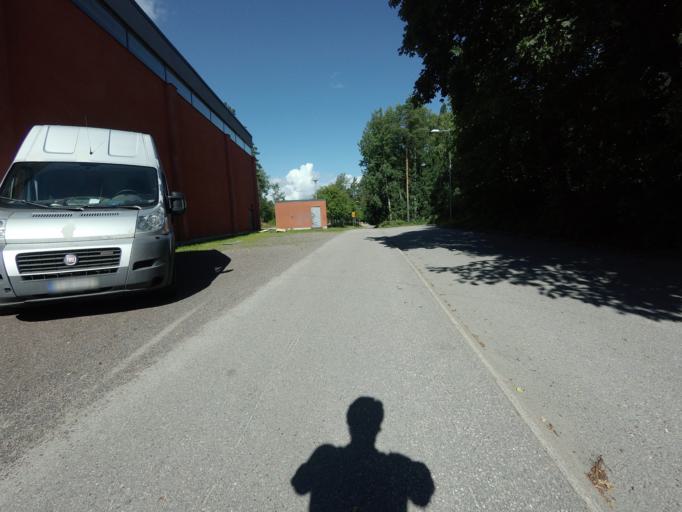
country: FI
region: Uusimaa
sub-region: Helsinki
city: Espoo
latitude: 60.1577
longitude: 24.6784
